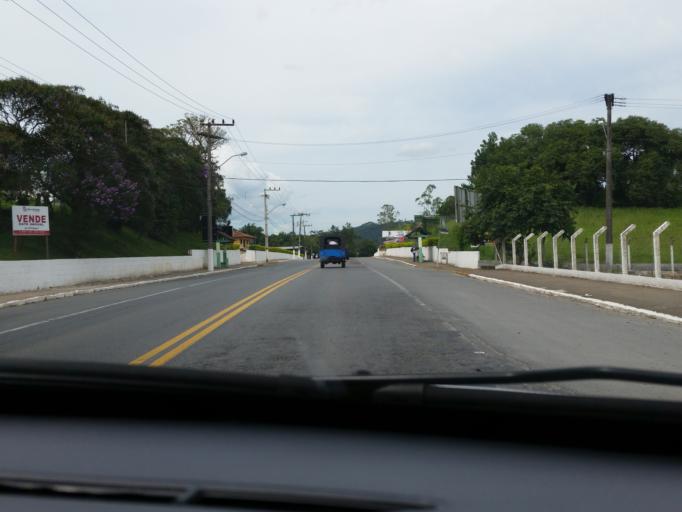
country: BR
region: Santa Catarina
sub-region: Rodeio
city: Gavea
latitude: -27.0300
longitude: -49.3827
